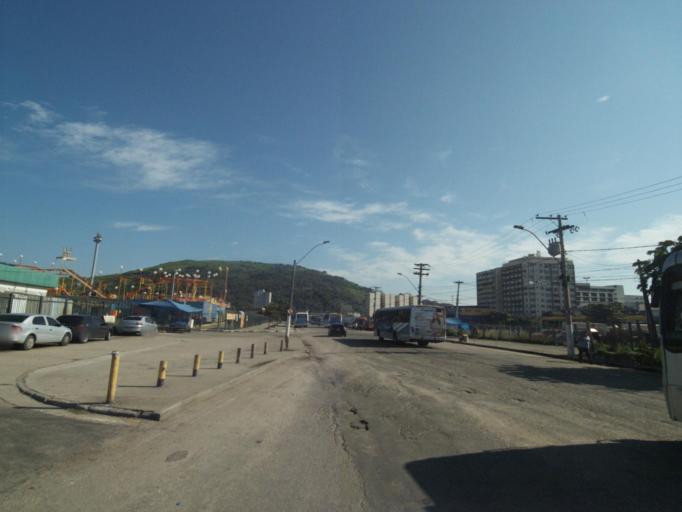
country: BR
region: Rio de Janeiro
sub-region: Niteroi
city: Niteroi
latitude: -22.8893
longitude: -43.1252
